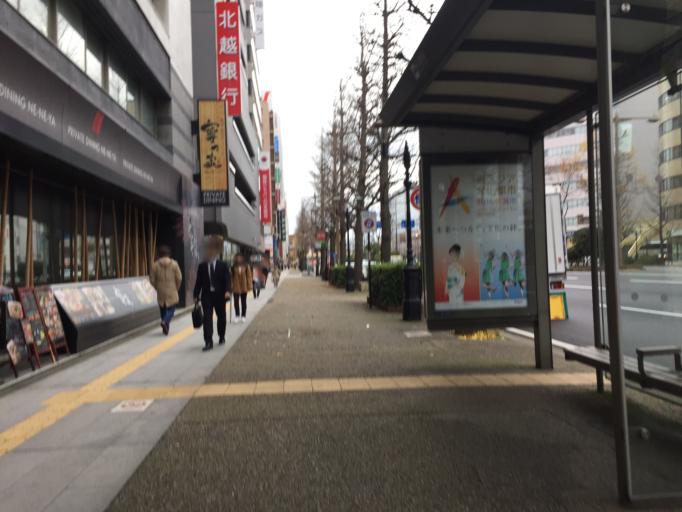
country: JP
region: Niigata
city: Niigata-shi
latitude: 37.9141
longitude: 139.0606
